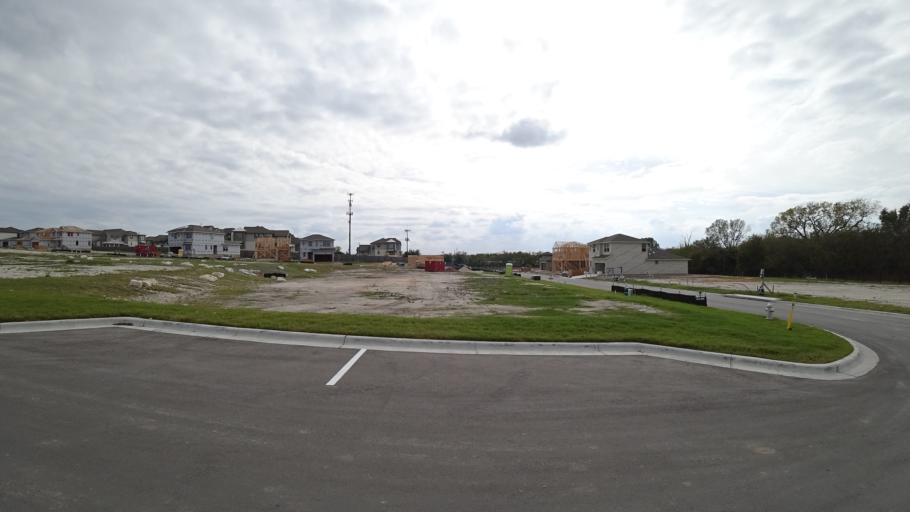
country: US
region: Texas
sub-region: Travis County
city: Wells Branch
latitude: 30.4485
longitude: -97.6727
